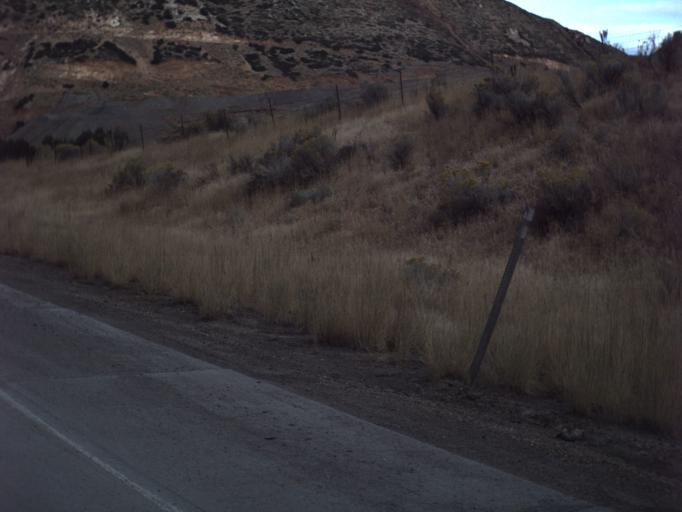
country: US
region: Utah
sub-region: Morgan County
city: Morgan
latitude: 41.0599
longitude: -111.5408
